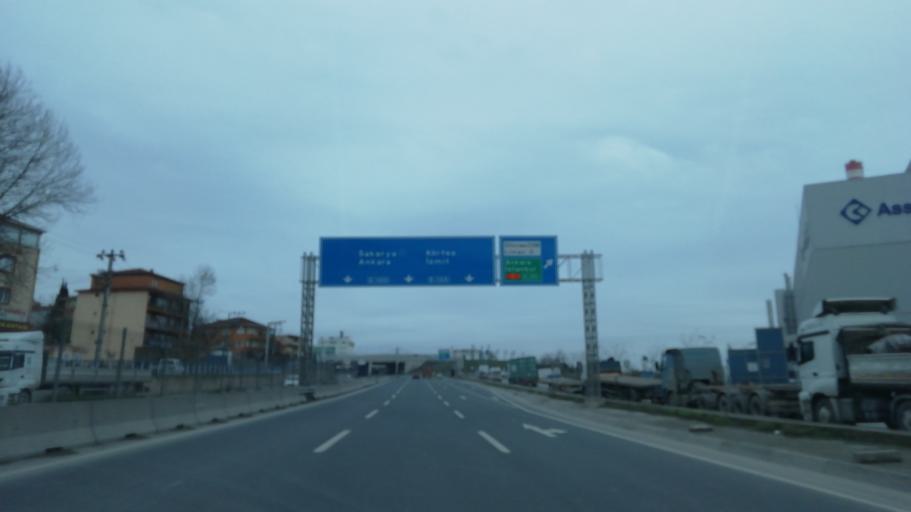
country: TR
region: Kocaeli
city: Tavsancil
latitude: 40.7822
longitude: 29.5384
